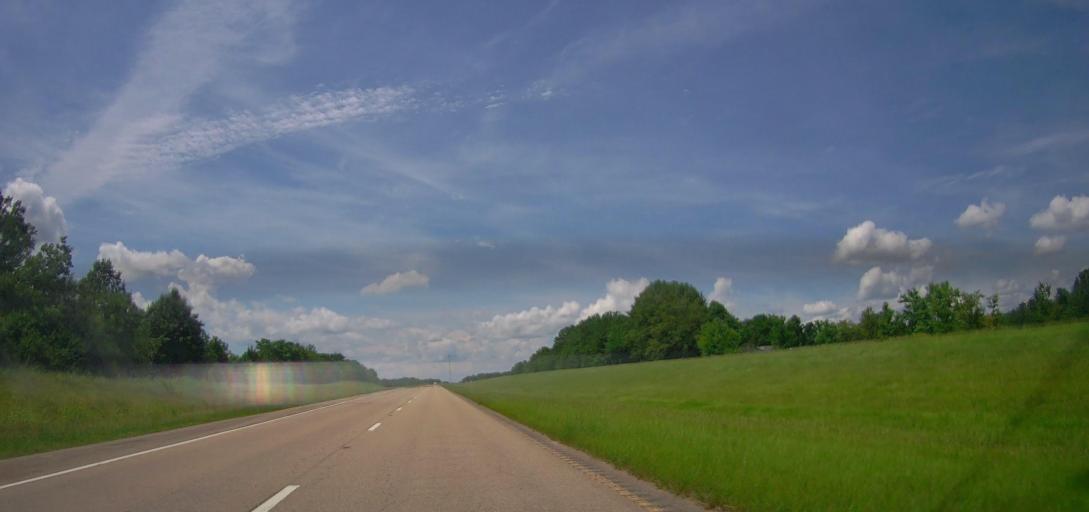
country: US
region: Mississippi
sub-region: Lee County
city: Nettleton
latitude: 33.9909
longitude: -88.6235
